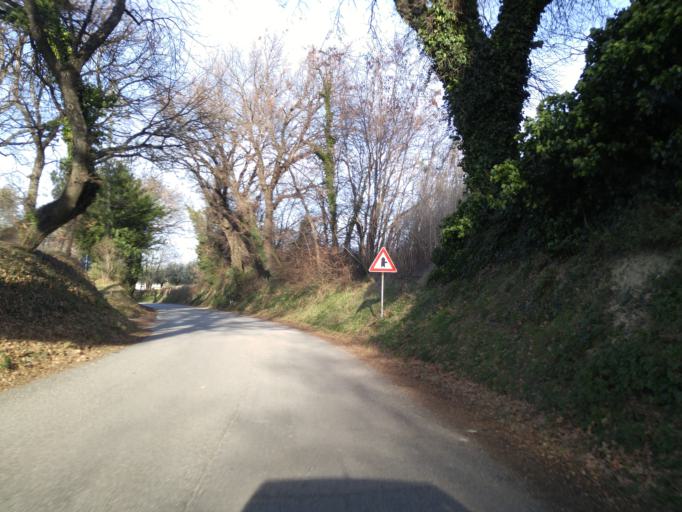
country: IT
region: The Marches
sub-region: Provincia di Pesaro e Urbino
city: Cartoceto
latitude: 43.7717
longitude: 12.8944
